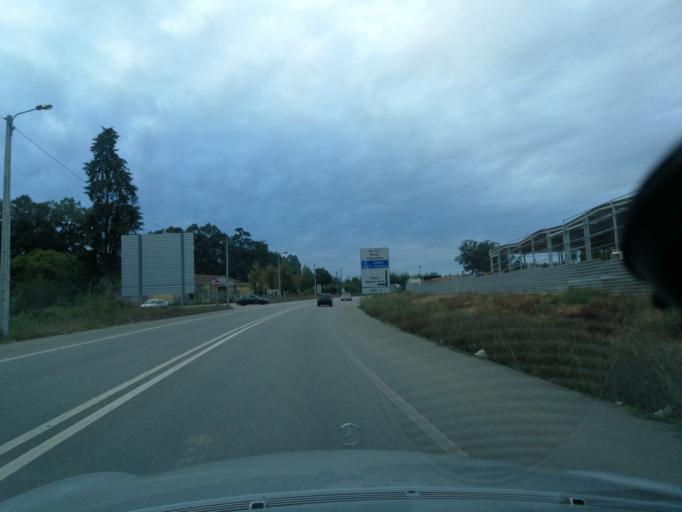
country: PT
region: Aveiro
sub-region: Albergaria-A-Velha
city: Albergaria-a-Velha
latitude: 40.6603
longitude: -8.4743
